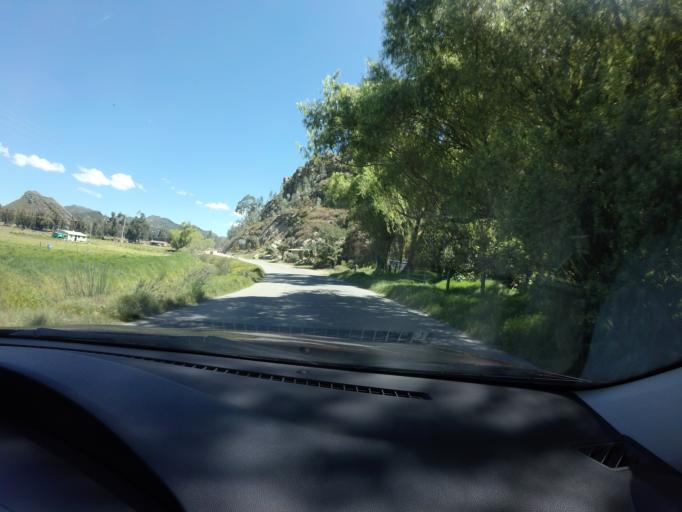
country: CO
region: Cundinamarca
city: Cucunuba
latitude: 5.2632
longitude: -73.7919
